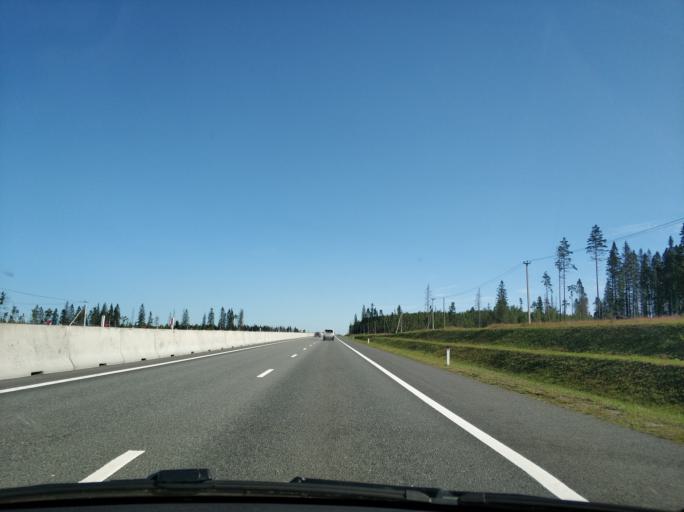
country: RU
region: Leningrad
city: Sosnovo
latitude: 60.4834
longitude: 30.1958
